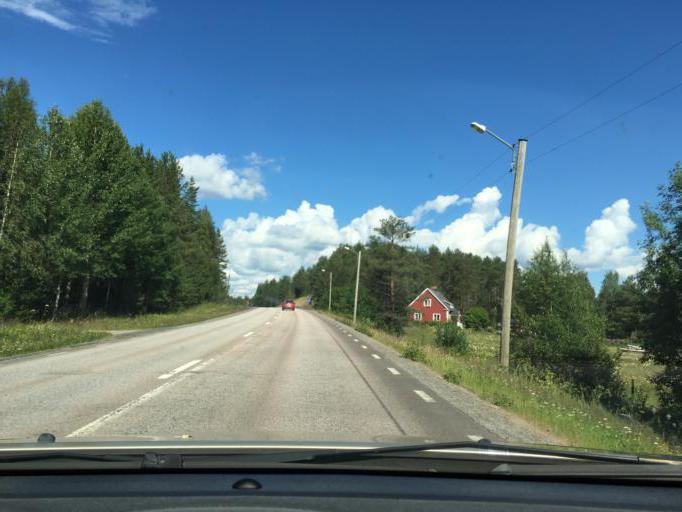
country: SE
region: Norrbotten
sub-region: Overkalix Kommun
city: OEverkalix
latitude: 66.2836
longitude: 22.8189
